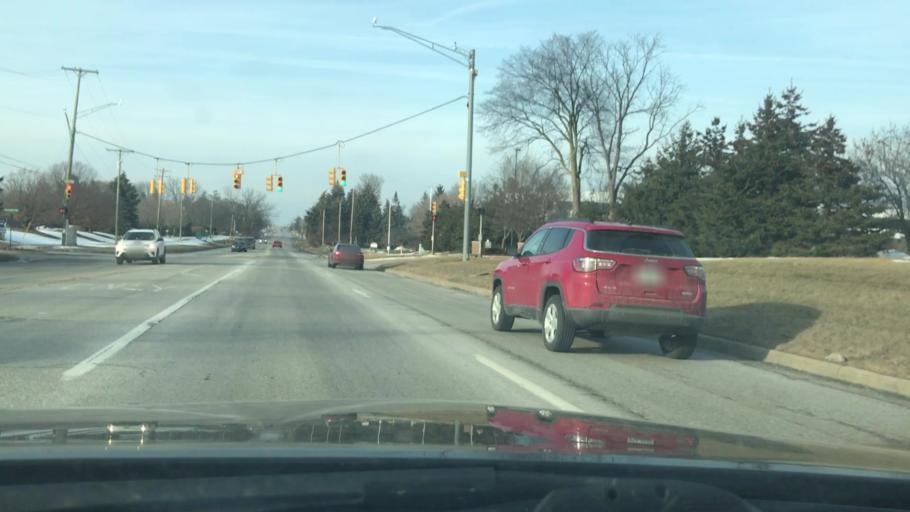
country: US
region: Michigan
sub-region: Wayne County
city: Northville
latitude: 42.4484
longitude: -83.4341
